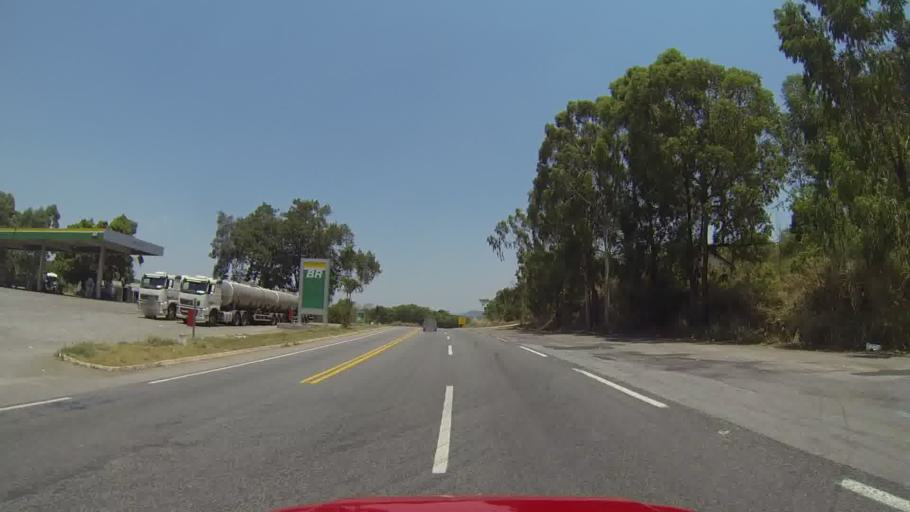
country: BR
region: Minas Gerais
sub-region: Itapecerica
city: Itapecerica
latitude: -20.2795
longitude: -45.1299
